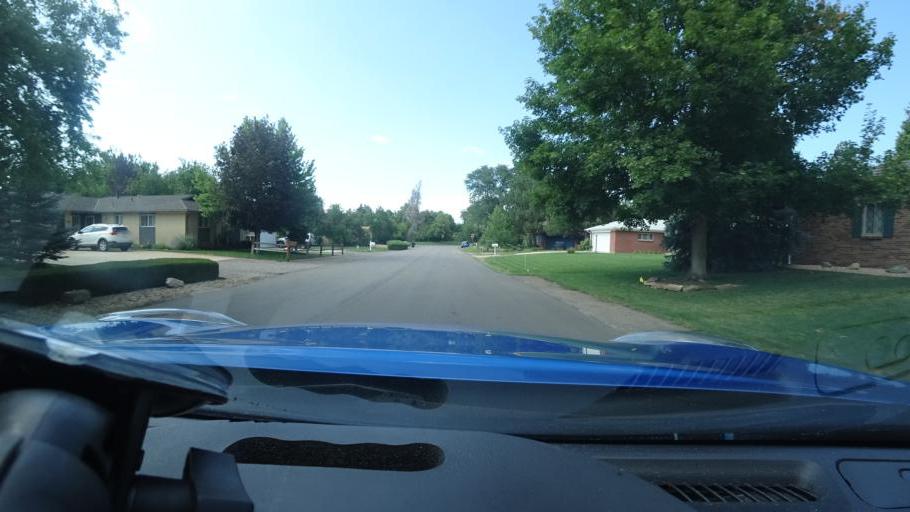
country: US
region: Colorado
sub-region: Adams County
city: Aurora
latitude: 39.6993
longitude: -104.8730
